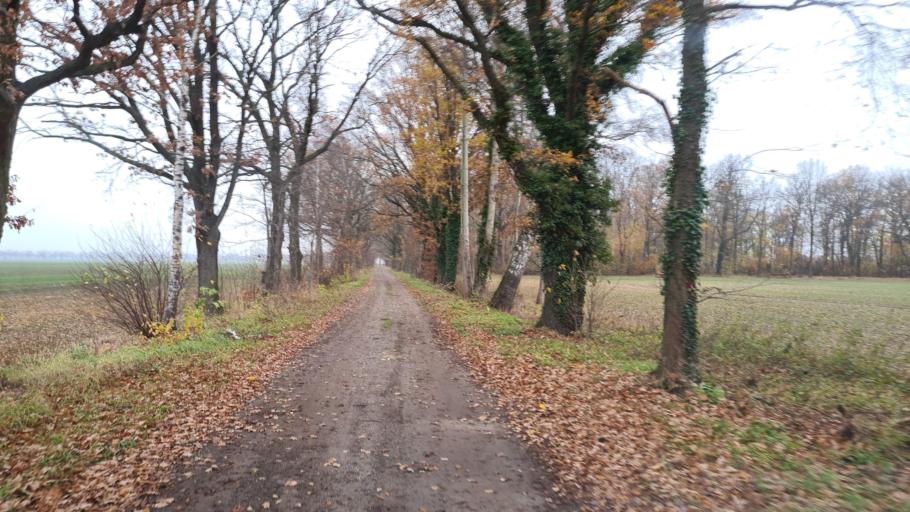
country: DE
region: Brandenburg
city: Lindenau
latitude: 51.4023
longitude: 13.7088
